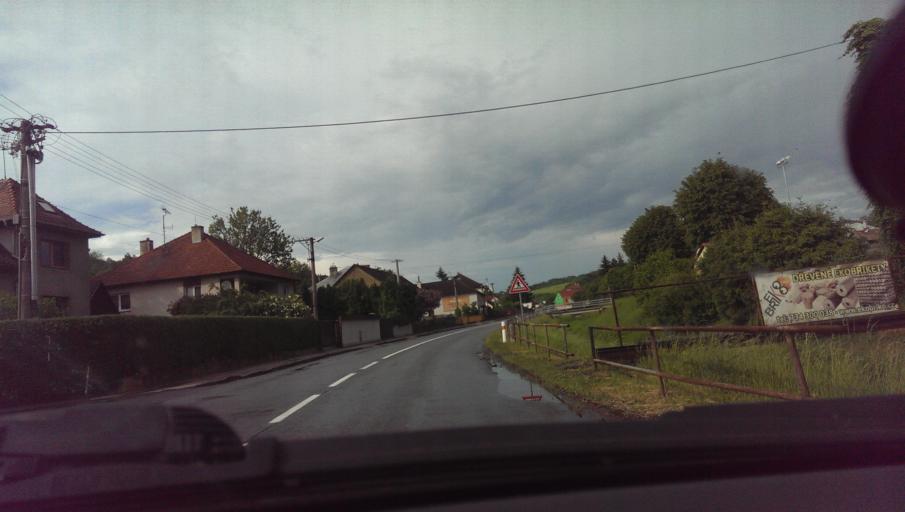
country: CZ
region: Zlin
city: Breznice
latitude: 49.1604
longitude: 17.6342
